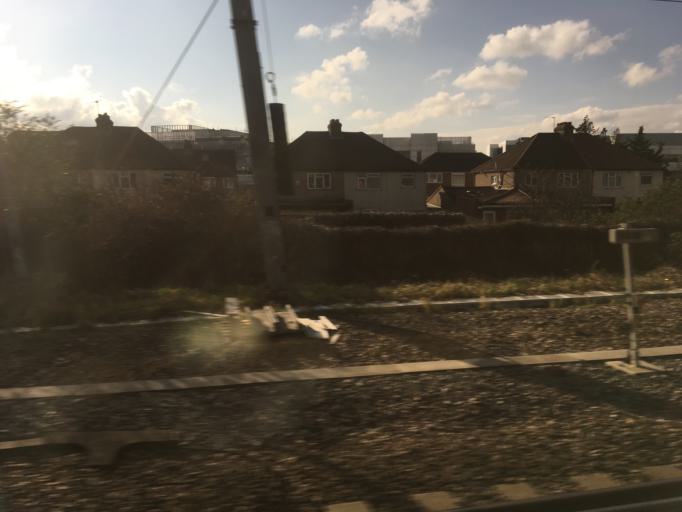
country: GB
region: England
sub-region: Greater London
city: Hayes
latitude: 51.5035
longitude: -0.4270
